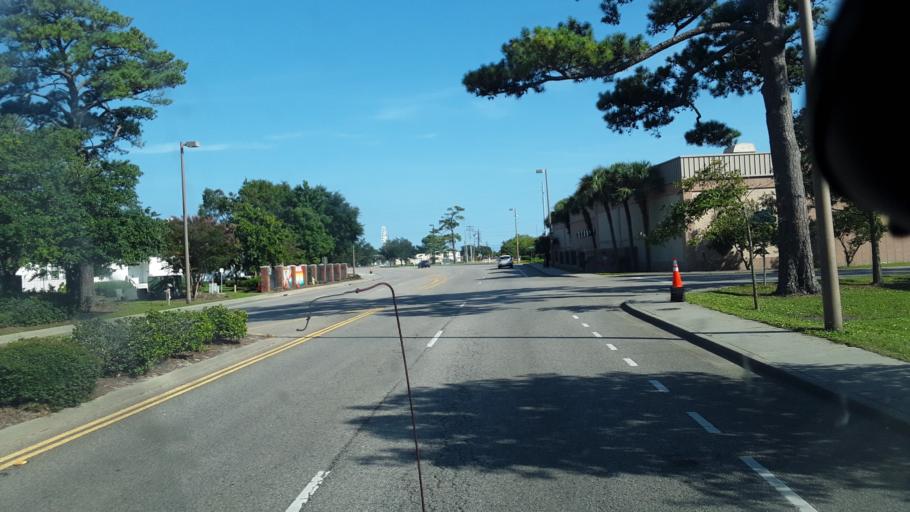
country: US
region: South Carolina
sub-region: Horry County
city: Myrtle Beach
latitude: 33.6992
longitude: -78.8855
